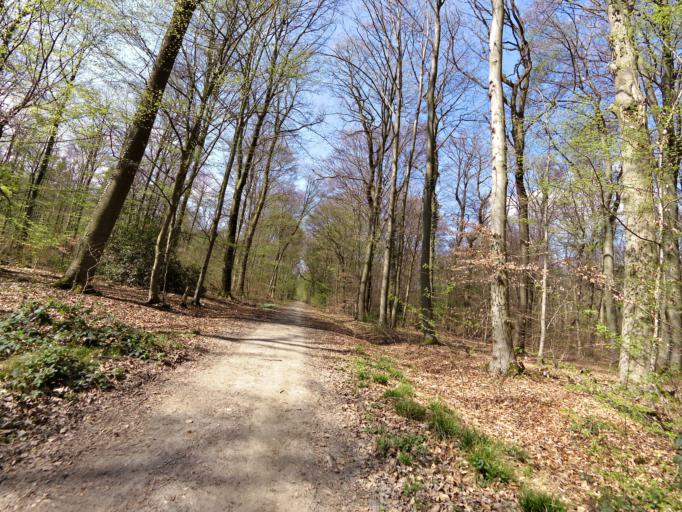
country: DE
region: North Rhine-Westphalia
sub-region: Regierungsbezirk Koln
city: Alfter
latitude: 50.6819
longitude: 7.0362
